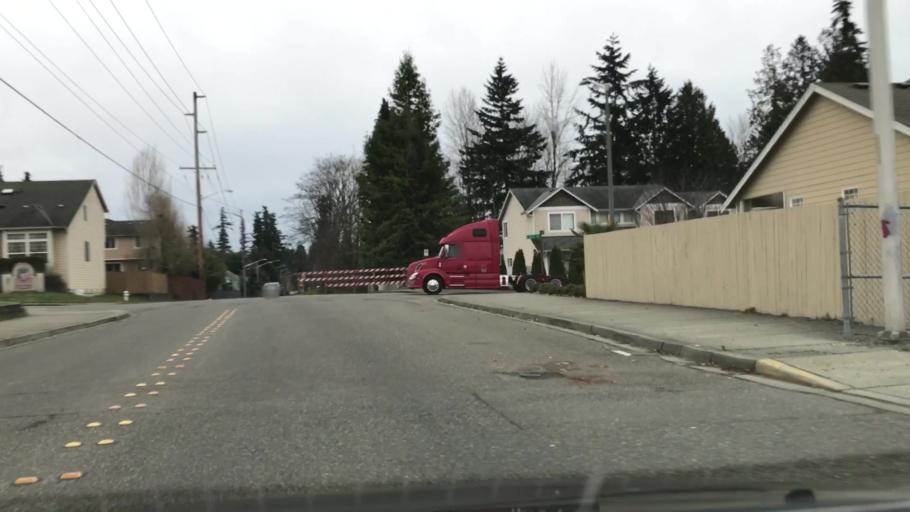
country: US
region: Washington
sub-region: King County
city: Kent
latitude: 47.3851
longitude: -122.2073
